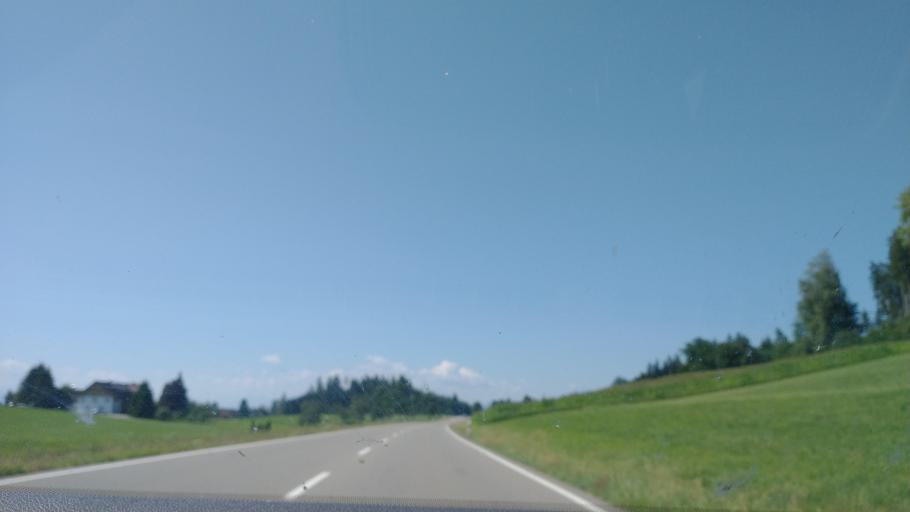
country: DE
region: Bavaria
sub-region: Swabia
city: Weissensberg
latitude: 47.6133
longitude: 9.7449
